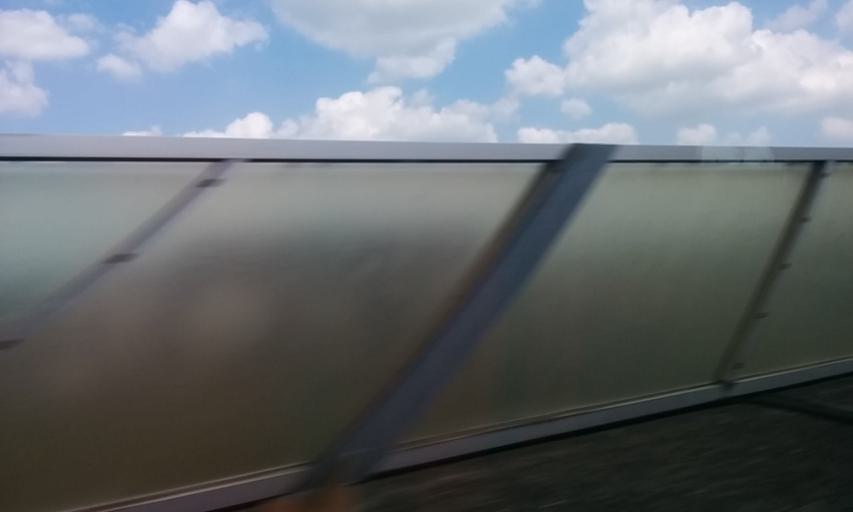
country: JP
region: Saitama
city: Kukichuo
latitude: 36.0539
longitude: 139.6720
